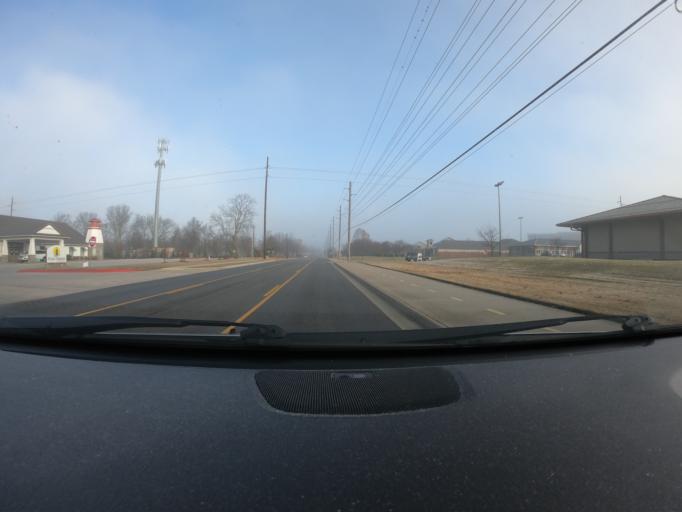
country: US
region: Arkansas
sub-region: Benton County
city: Bentonville
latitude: 36.3616
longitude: -94.2219
